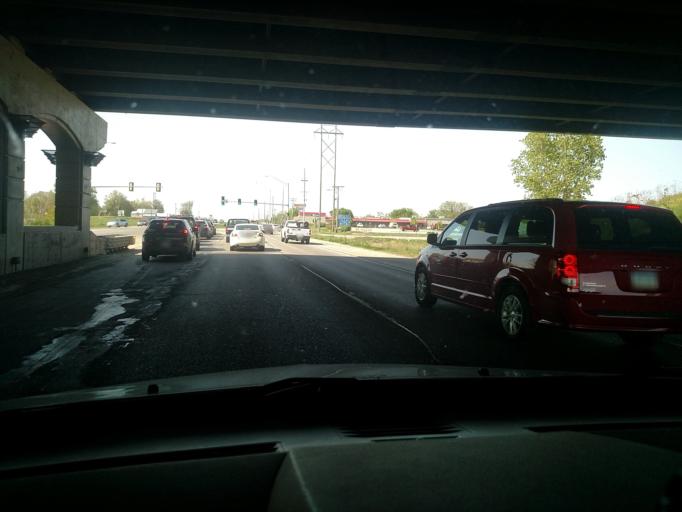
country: US
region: Iowa
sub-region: Polk County
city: Saylorville
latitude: 41.6494
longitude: -93.6200
